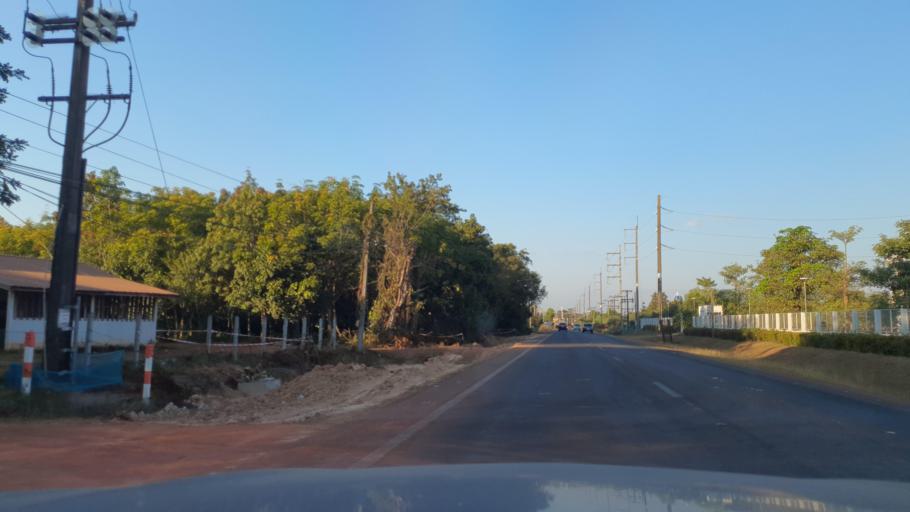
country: TH
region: Nakhon Phanom
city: Si Songkhram
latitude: 17.5787
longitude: 104.2327
